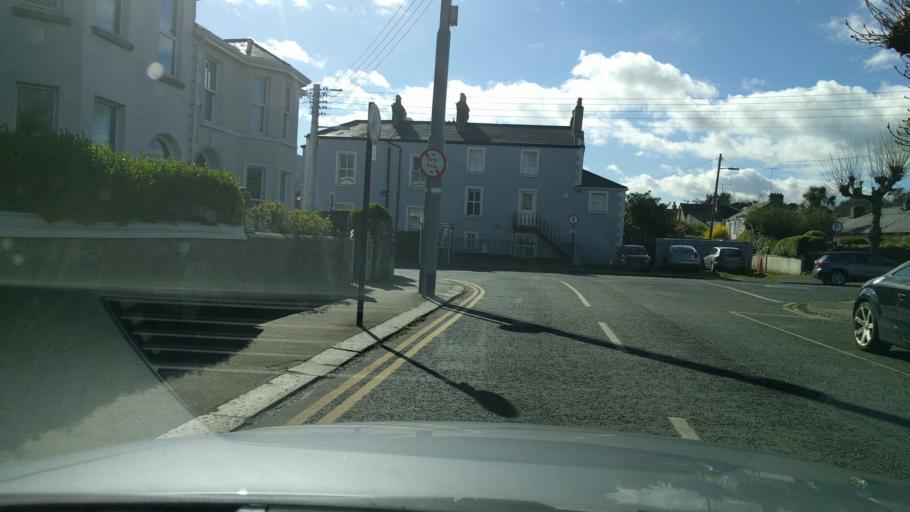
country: IE
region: Leinster
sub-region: Wicklow
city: Bray
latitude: 53.2030
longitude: -6.1013
